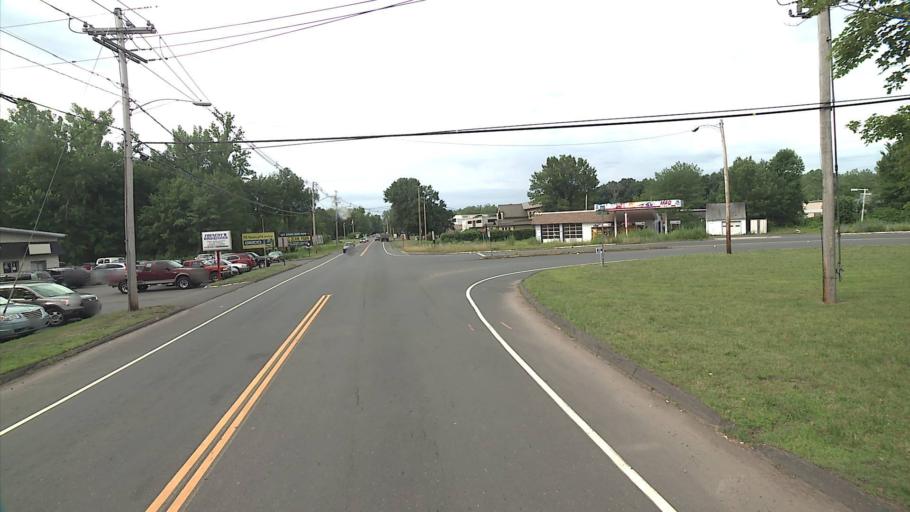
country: US
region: Connecticut
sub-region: New Haven County
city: Meriden
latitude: 41.4975
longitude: -72.8146
